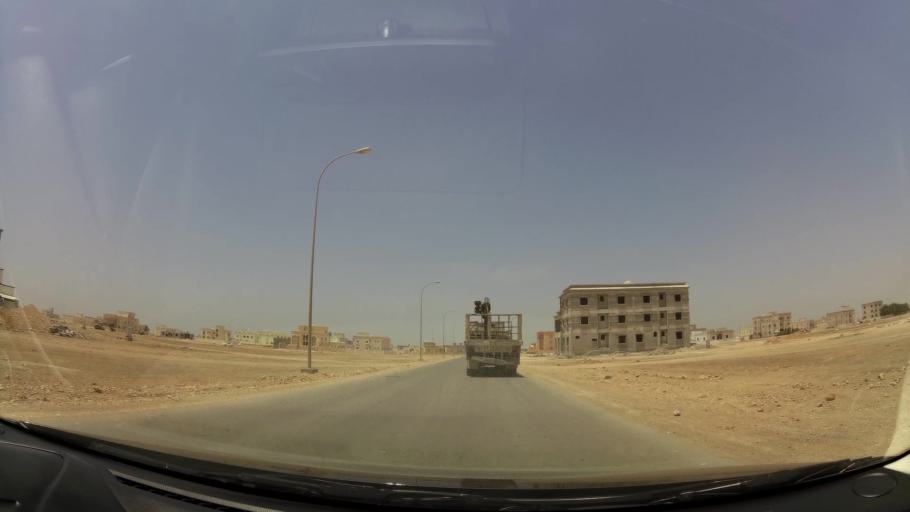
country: OM
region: Zufar
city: Salalah
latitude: 17.0933
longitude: 54.2106
